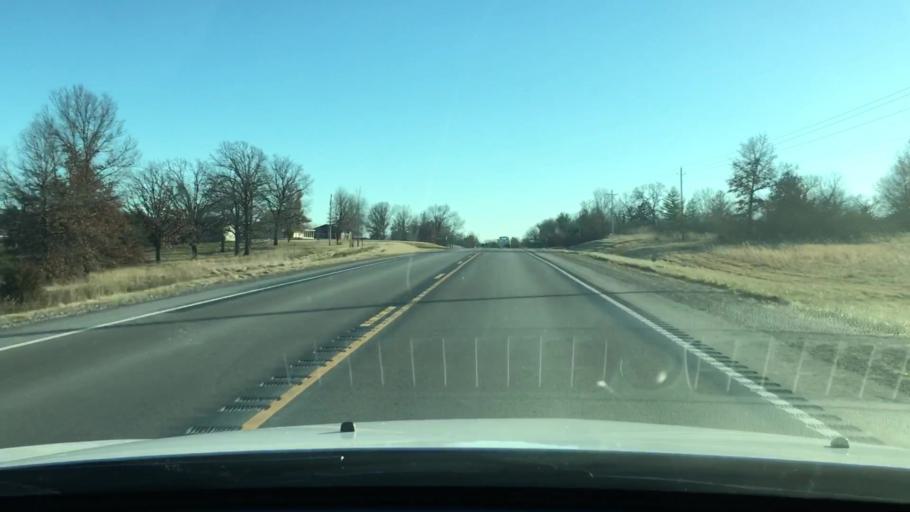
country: US
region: Missouri
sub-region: Boone County
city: Centralia
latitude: 39.1709
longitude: -92.1777
